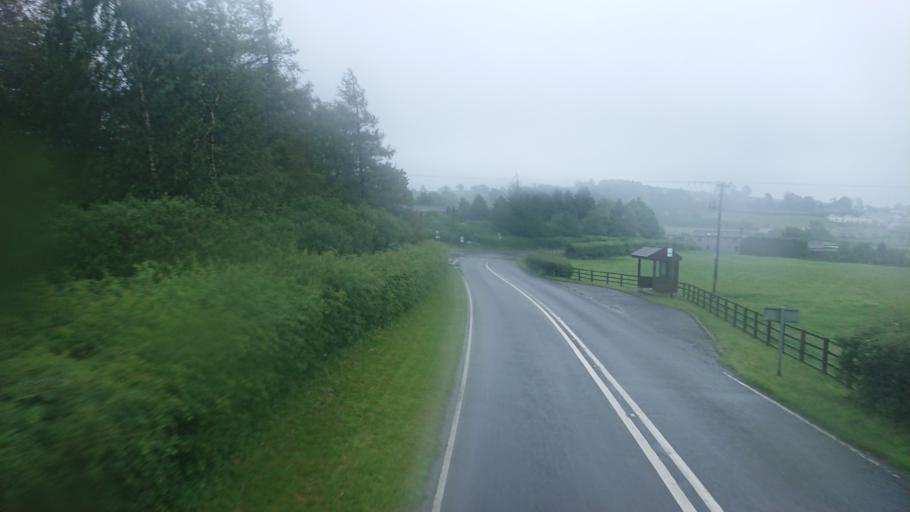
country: GB
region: England
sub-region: Cumbria
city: Milnthorpe
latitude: 54.1921
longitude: -2.7214
